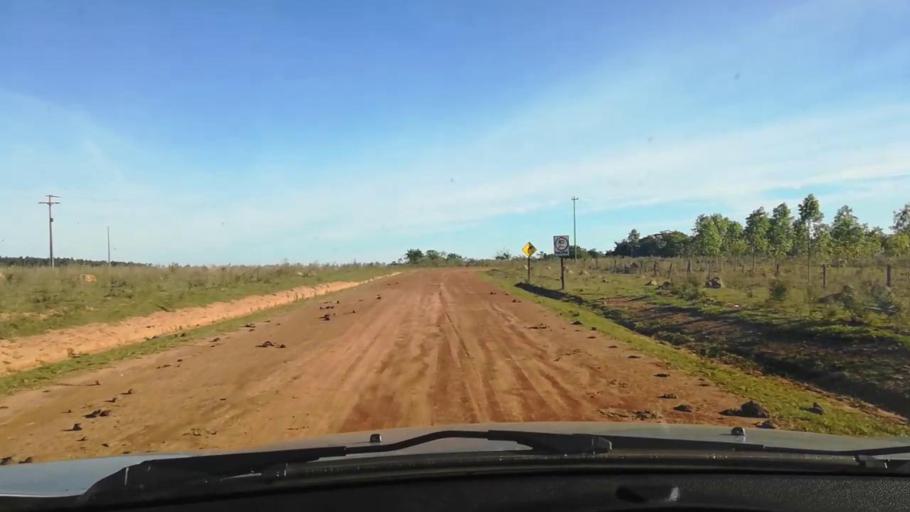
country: PY
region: Caaguazu
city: Coronel Oviedo
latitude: -25.5174
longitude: -56.4102
